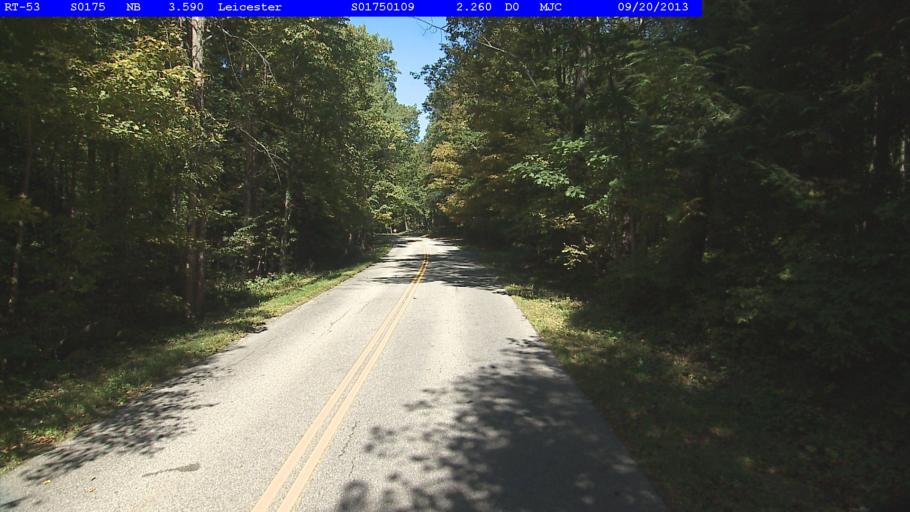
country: US
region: Vermont
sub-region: Rutland County
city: Brandon
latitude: 43.8754
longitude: -73.0637
